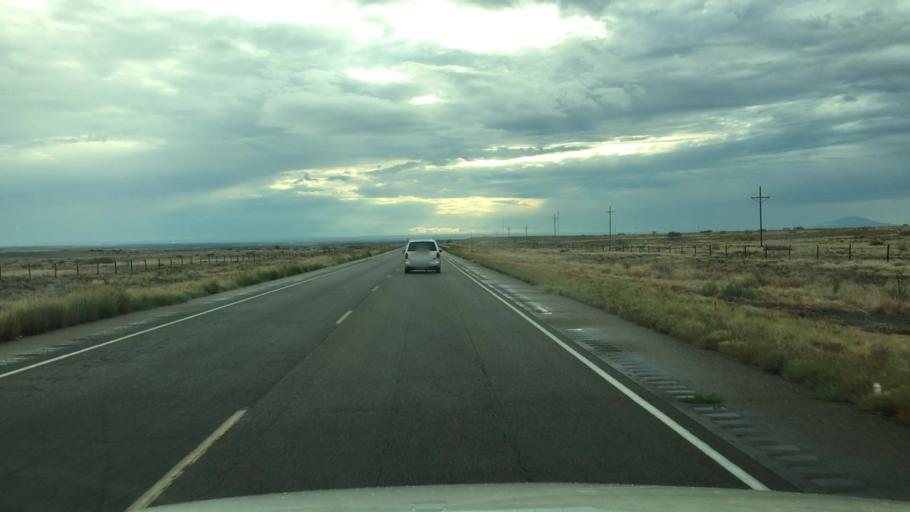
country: US
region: New Mexico
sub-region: Chaves County
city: Roswell
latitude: 33.4007
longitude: -104.3378
